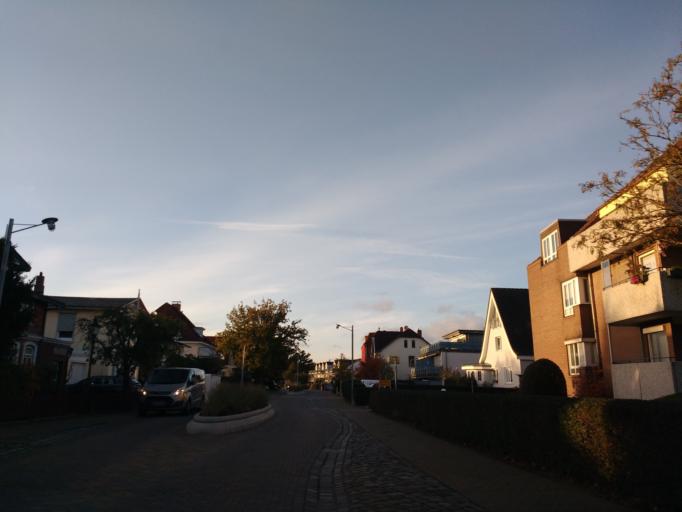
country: DE
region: Schleswig-Holstein
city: Kellenhusen
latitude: 54.1908
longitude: 11.0593
